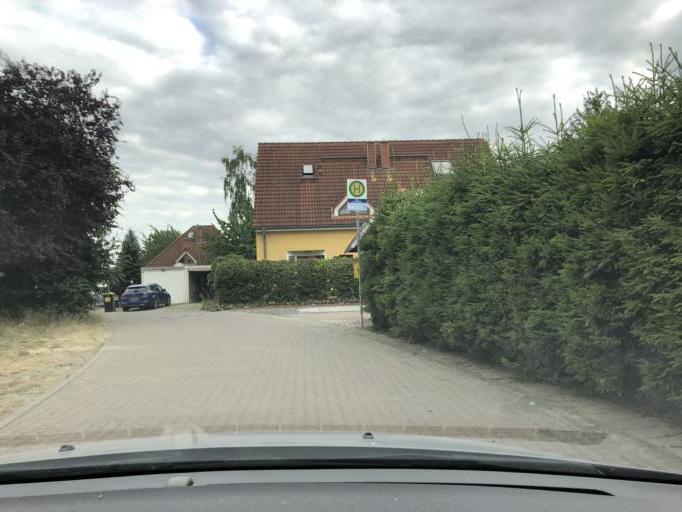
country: DE
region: Saxony
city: Frohburg
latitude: 51.0242
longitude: 12.6172
